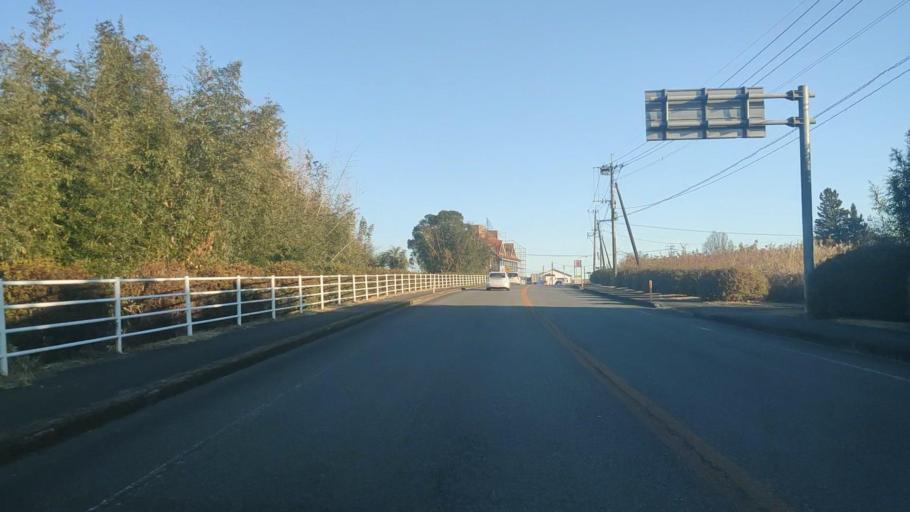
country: JP
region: Miyazaki
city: Takanabe
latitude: 32.1940
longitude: 131.5245
